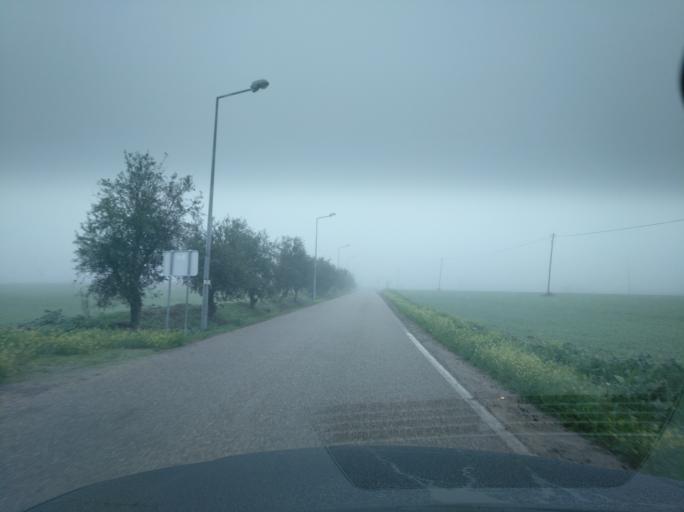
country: PT
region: Portalegre
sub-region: Campo Maior
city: Campo Maior
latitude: 39.0232
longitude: -7.0680
